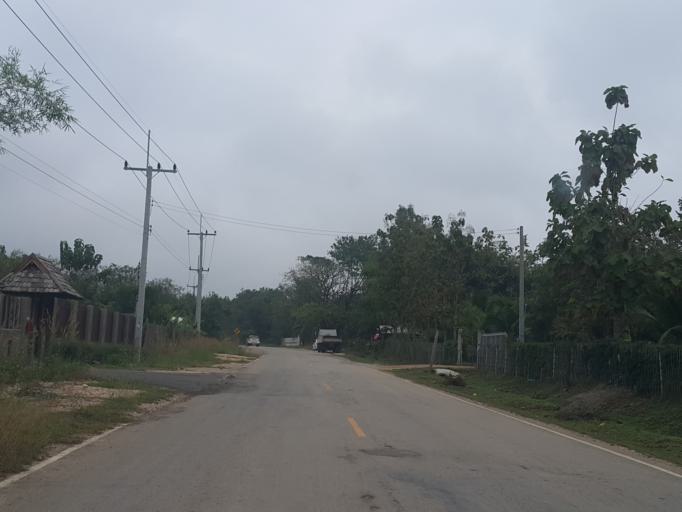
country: TH
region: Lampang
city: Lampang
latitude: 18.3319
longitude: 99.4865
